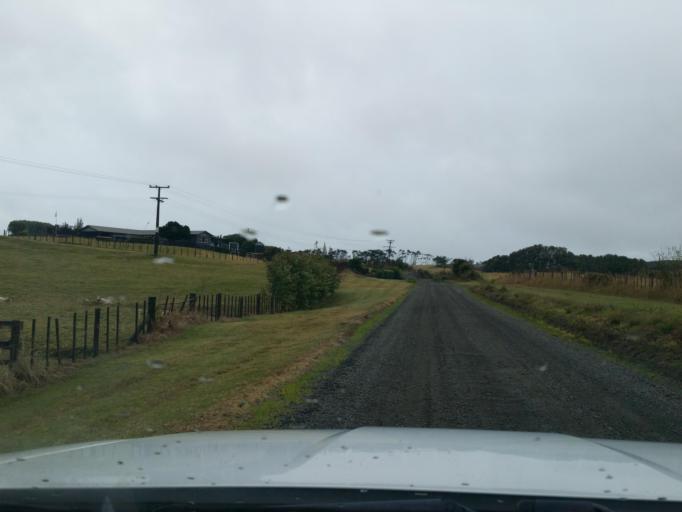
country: NZ
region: Northland
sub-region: Kaipara District
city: Dargaville
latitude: -36.0563
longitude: 173.8586
